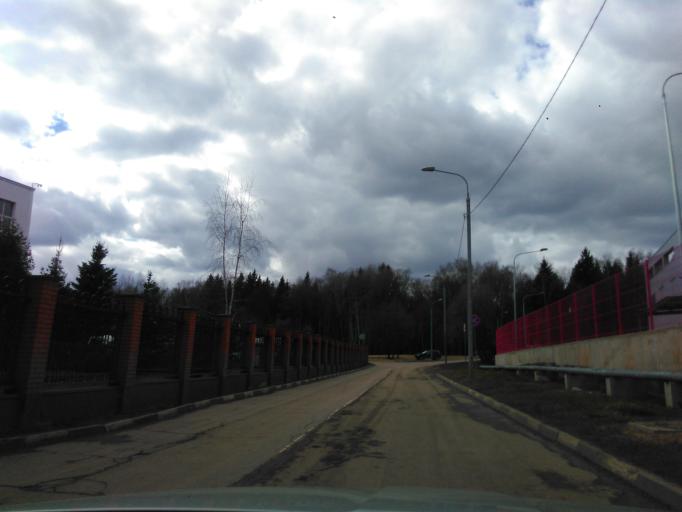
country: RU
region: Moscow
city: Zelenograd
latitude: 55.9775
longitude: 37.2152
